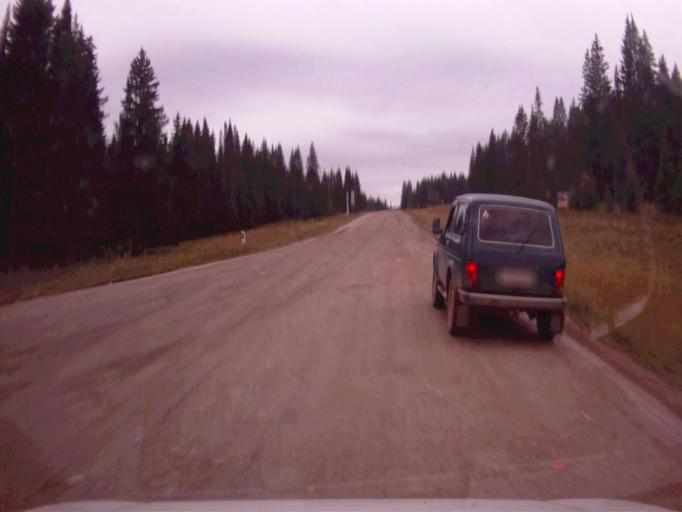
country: RU
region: Chelyabinsk
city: Nyazepetrovsk
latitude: 56.0599
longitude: 59.5615
